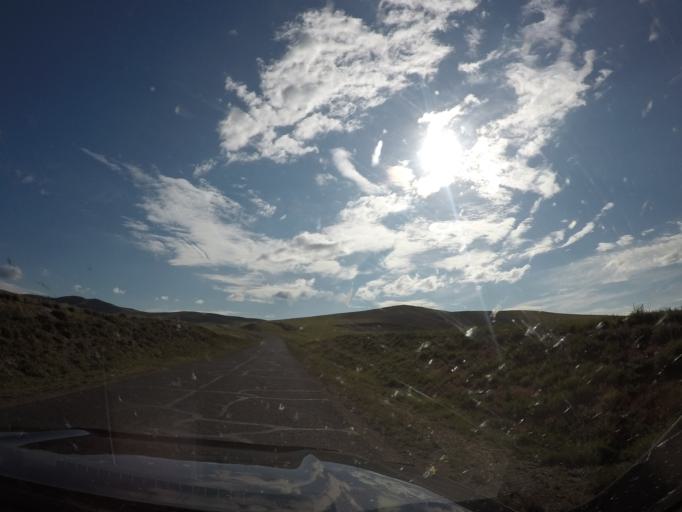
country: MN
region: Hentiy
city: Modot
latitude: 47.8024
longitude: 108.7781
